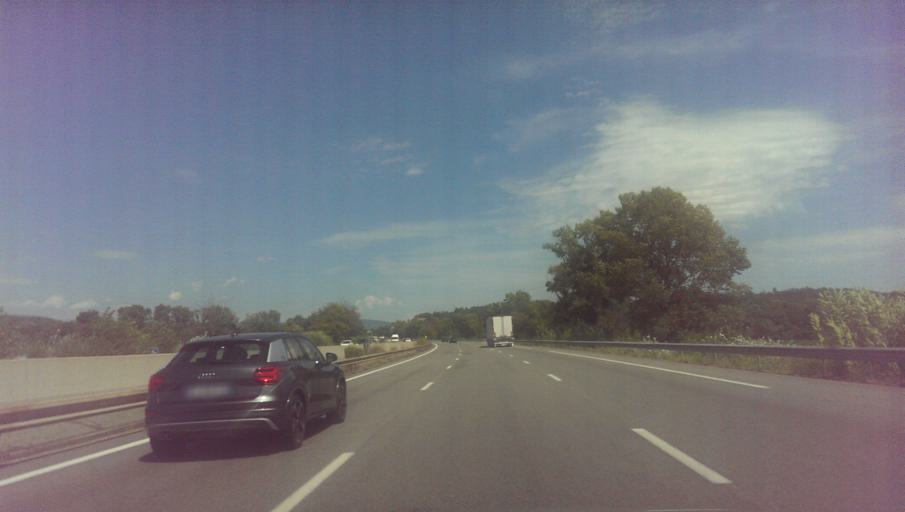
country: FR
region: Provence-Alpes-Cote d'Azur
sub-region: Departement du Var
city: Les Arcs
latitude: 43.4439
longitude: 6.4912
